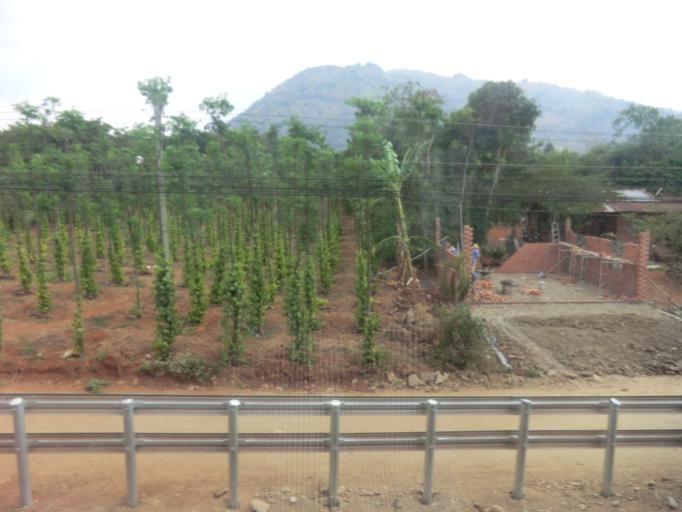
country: VN
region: Dong Nai
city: Gia Ray
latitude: 10.9704
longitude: 107.3851
